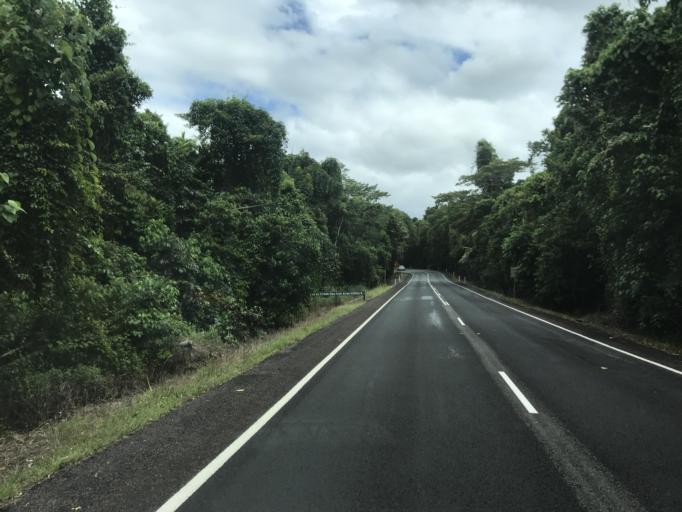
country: AU
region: Queensland
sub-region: Cassowary Coast
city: Innisfail
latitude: -17.8551
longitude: 146.0658
